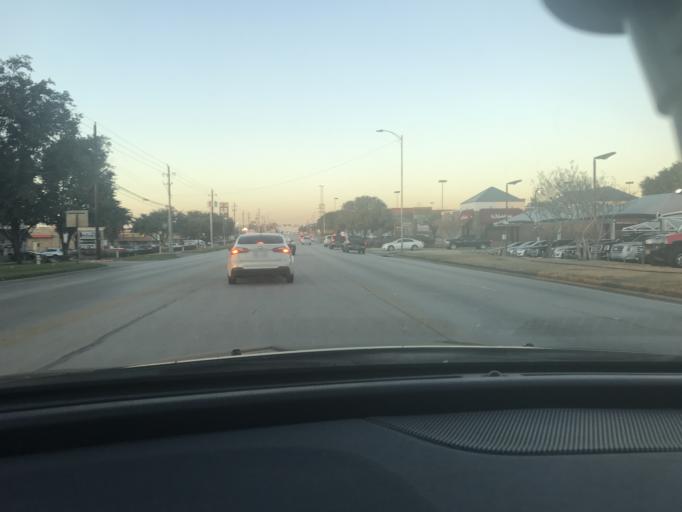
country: US
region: Texas
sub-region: Tarrant County
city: Arlington
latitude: 32.7667
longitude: -97.0971
